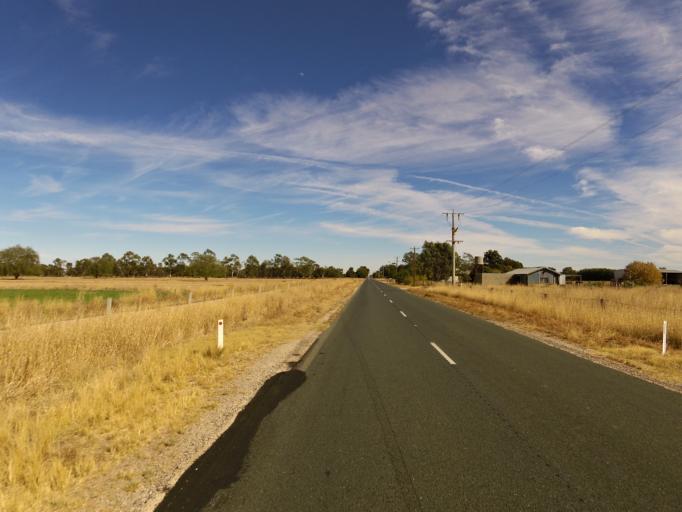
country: AU
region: Victoria
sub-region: Campaspe
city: Echuca
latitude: -36.2990
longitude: 144.5178
